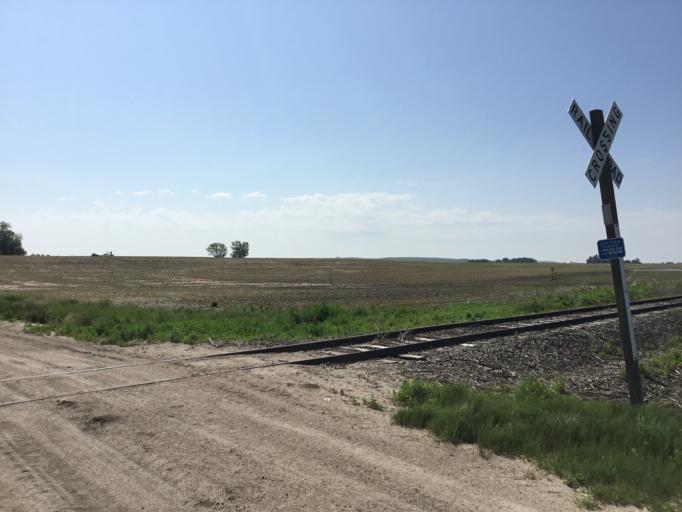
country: US
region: Kansas
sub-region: Cloud County
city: Concordia
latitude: 39.7118
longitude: -97.7761
